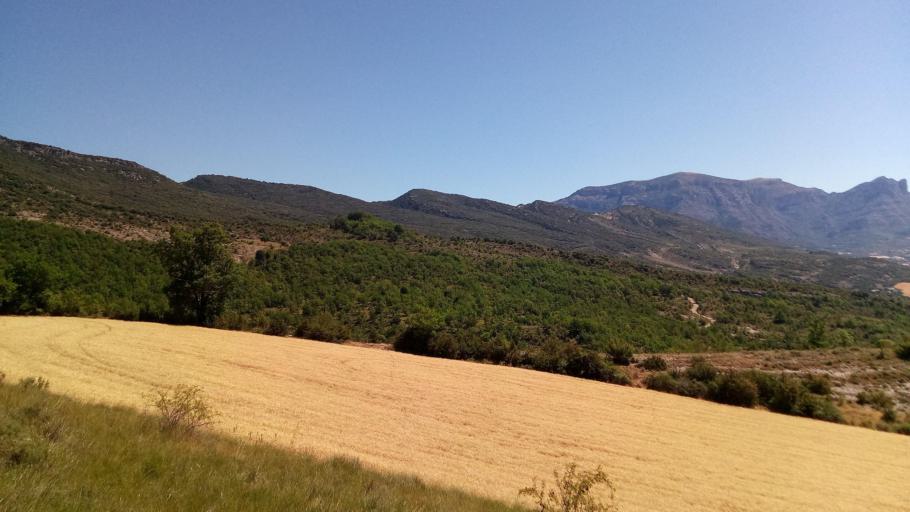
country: ES
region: Aragon
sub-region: Provincia de Huesca
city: Lascuarre
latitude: 42.3168
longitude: 0.4966
